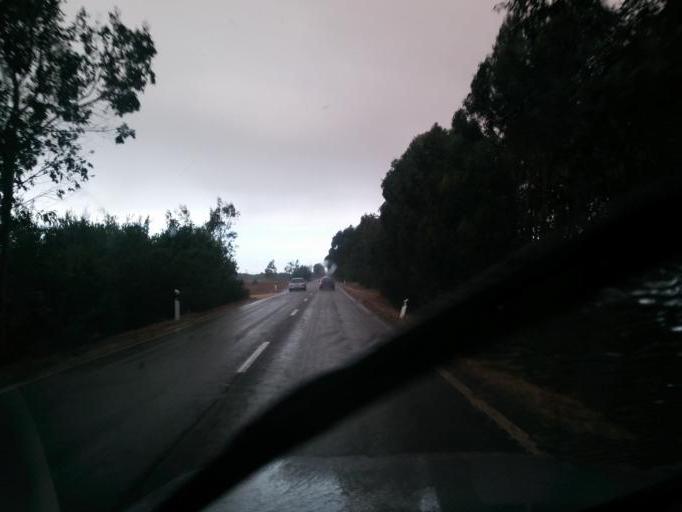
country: PT
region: Beja
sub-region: Odemira
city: Vila Nova de Milfontes
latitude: 37.6844
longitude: -8.7645
